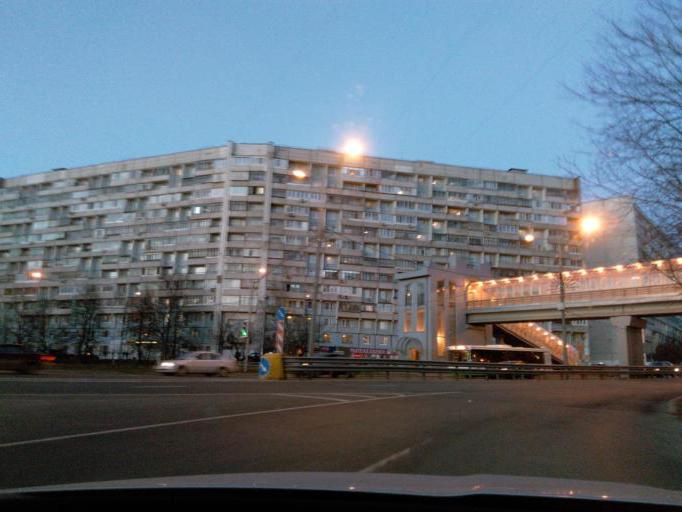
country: RU
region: Moscow
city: Zelenograd
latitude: 55.9823
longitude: 37.1785
